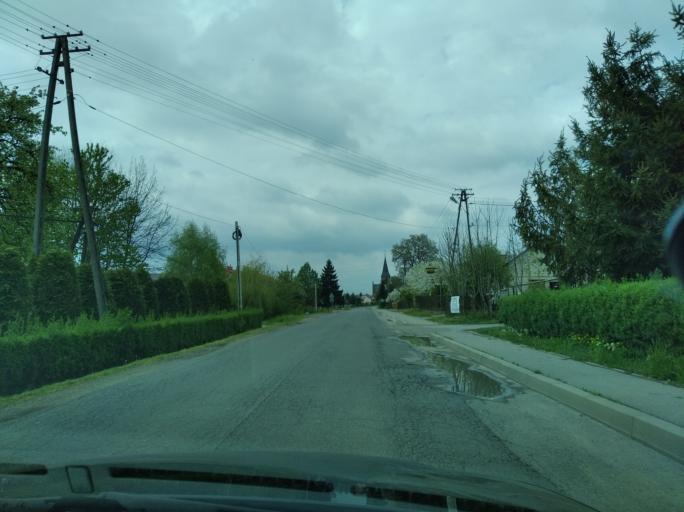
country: PL
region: Subcarpathian Voivodeship
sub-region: Powiat brzozowski
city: Jasionow
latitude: 49.6449
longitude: 21.9448
